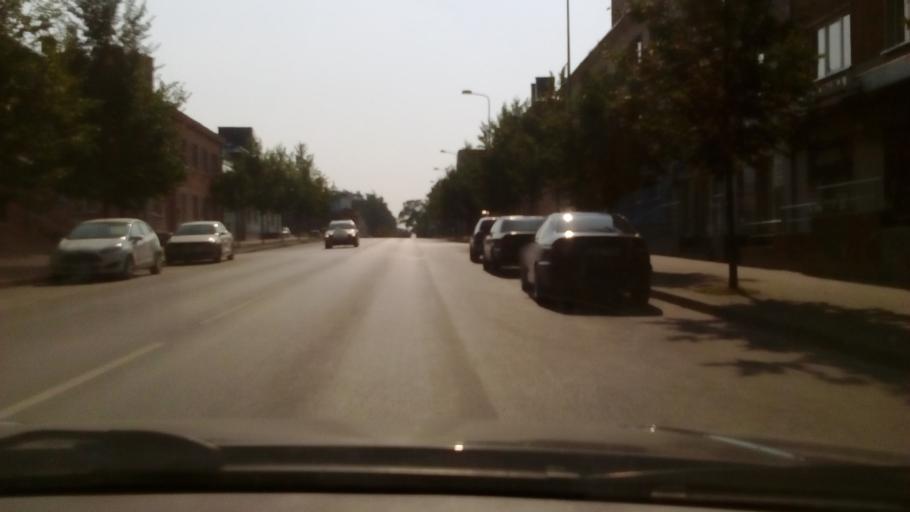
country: LT
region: Alytaus apskritis
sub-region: Alytus
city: Alytus
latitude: 54.3982
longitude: 24.0484
